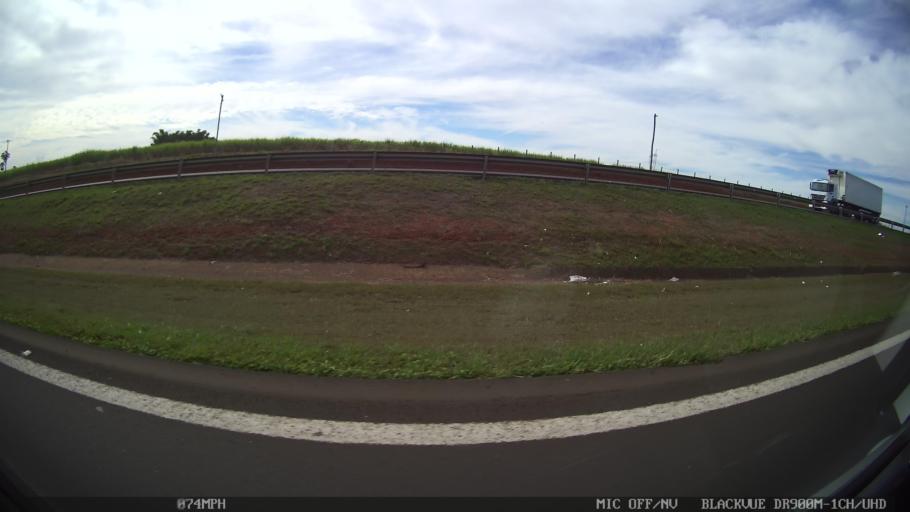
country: BR
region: Sao Paulo
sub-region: Taquaritinga
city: Taquaritinga
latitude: -21.5432
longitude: -48.5007
